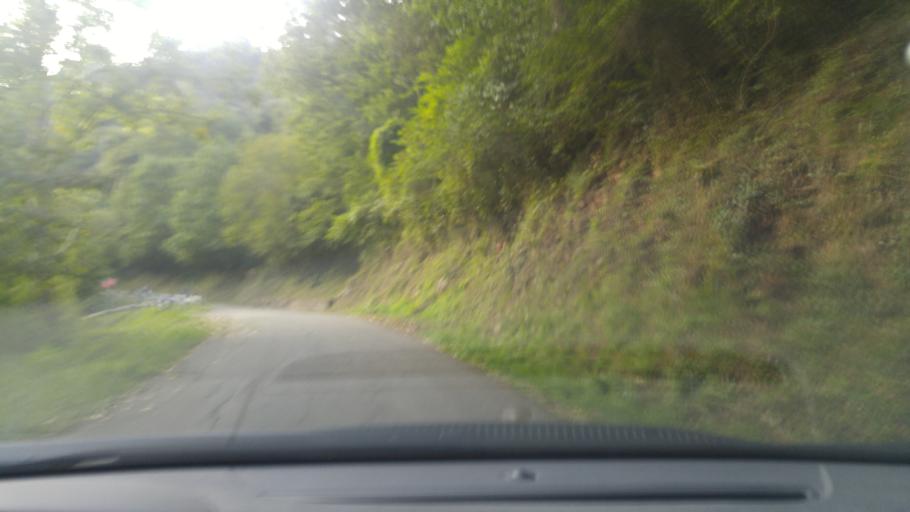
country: ES
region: Asturias
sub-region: Province of Asturias
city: Proaza
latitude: 43.2461
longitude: -6.0343
